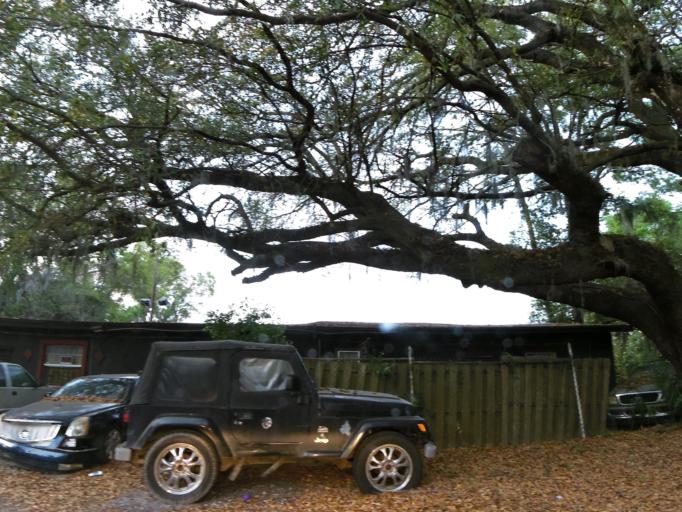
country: US
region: Florida
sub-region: Duval County
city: Jacksonville
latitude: 30.3633
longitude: -81.6361
